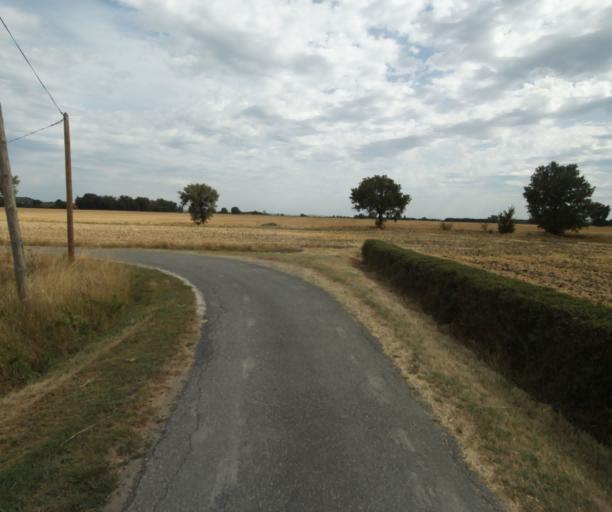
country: FR
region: Midi-Pyrenees
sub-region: Departement de la Haute-Garonne
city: Saint-Felix-Lauragais
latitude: 43.4333
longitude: 1.9266
